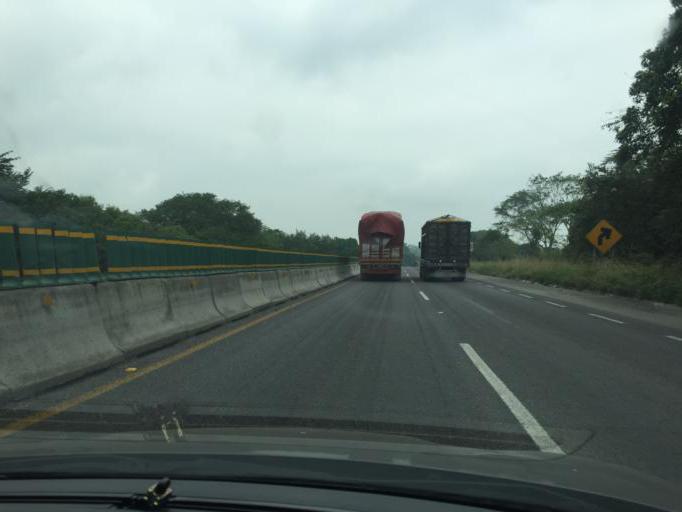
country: MX
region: Veracruz
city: Villa Nanchital
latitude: 18.0548
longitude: -94.3307
